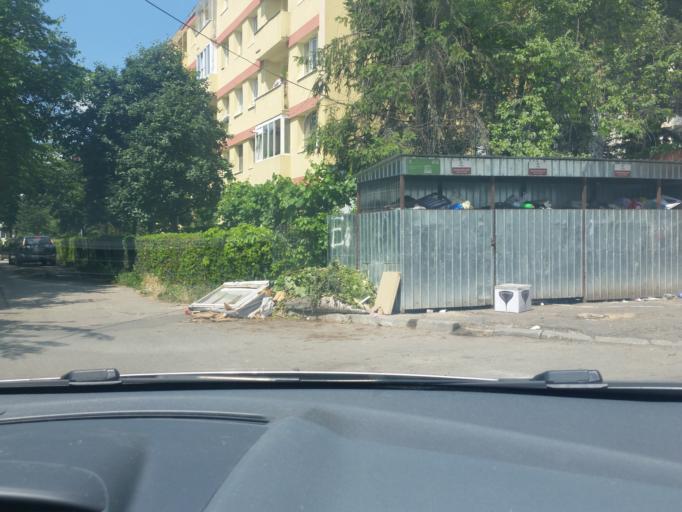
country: RO
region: Cluj
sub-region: Municipiul Cluj-Napoca
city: Cluj-Napoca
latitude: 46.7718
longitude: 23.5587
